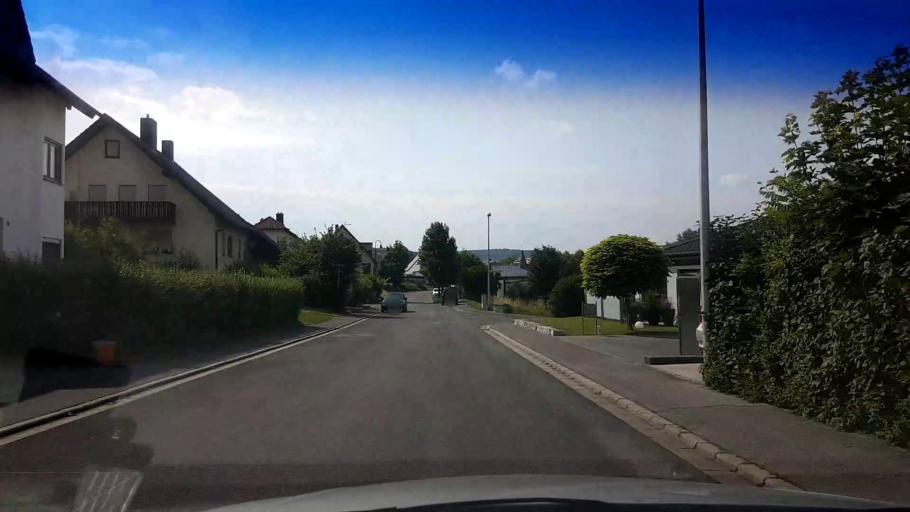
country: DE
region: Bavaria
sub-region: Upper Franconia
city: Viereth-Trunstadt
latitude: 49.9251
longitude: 10.7541
